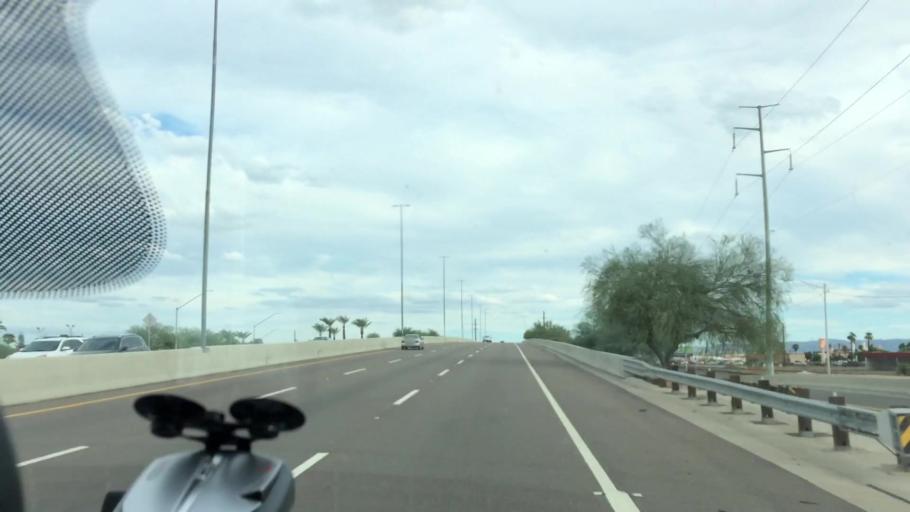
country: US
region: Arizona
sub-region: Maricopa County
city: Glendale
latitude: 33.5123
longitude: -112.1556
